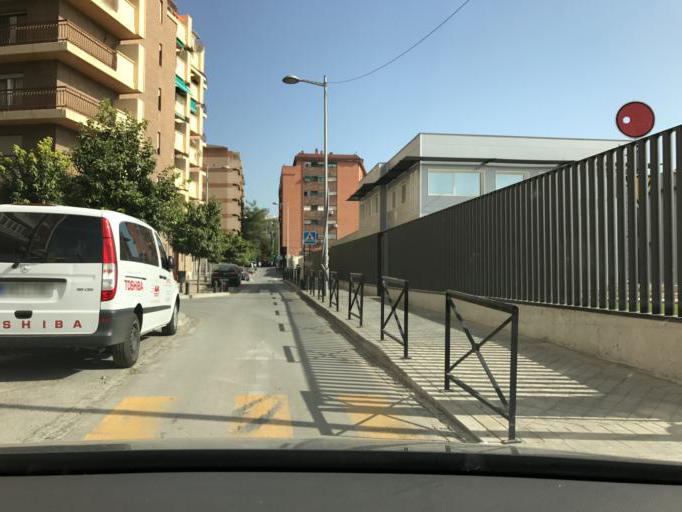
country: ES
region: Andalusia
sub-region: Provincia de Granada
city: Granada
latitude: 37.1841
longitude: -3.6085
